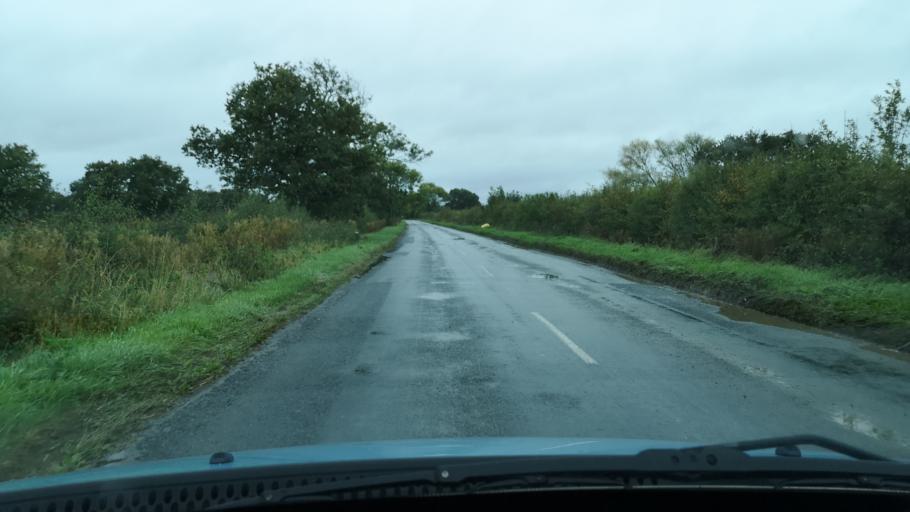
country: GB
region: England
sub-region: Doncaster
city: Moss
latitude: 53.6219
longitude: -1.0806
